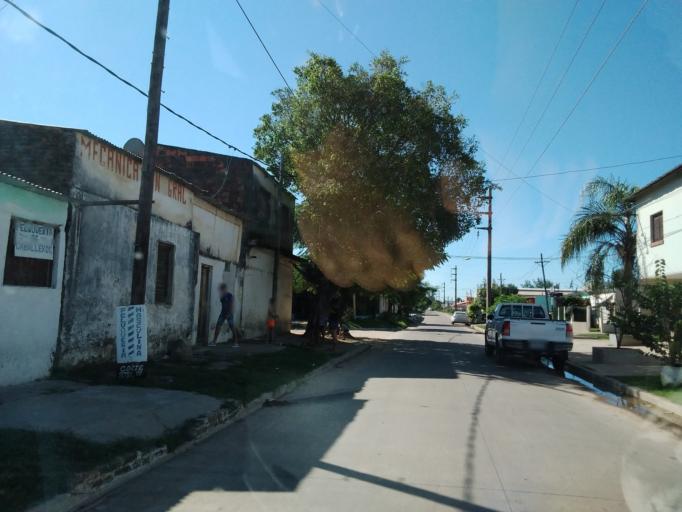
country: AR
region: Corrientes
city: Corrientes
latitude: -27.4738
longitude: -58.7932
